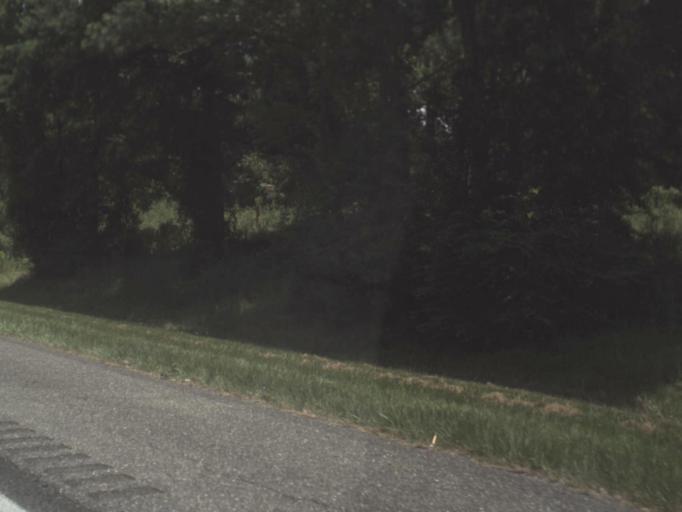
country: US
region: Florida
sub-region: Madison County
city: Madison
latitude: 30.4306
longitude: -83.5824
